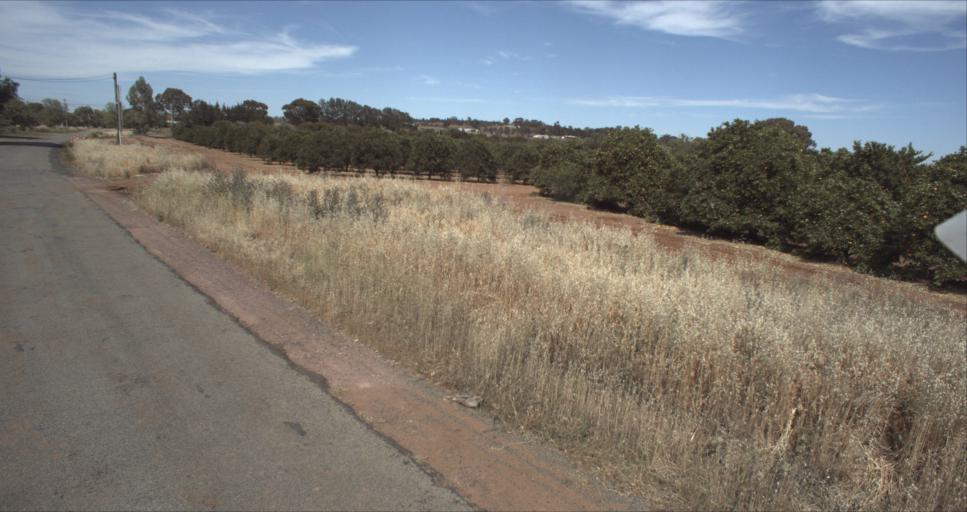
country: AU
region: New South Wales
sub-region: Leeton
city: Leeton
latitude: -34.5690
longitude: 146.4561
